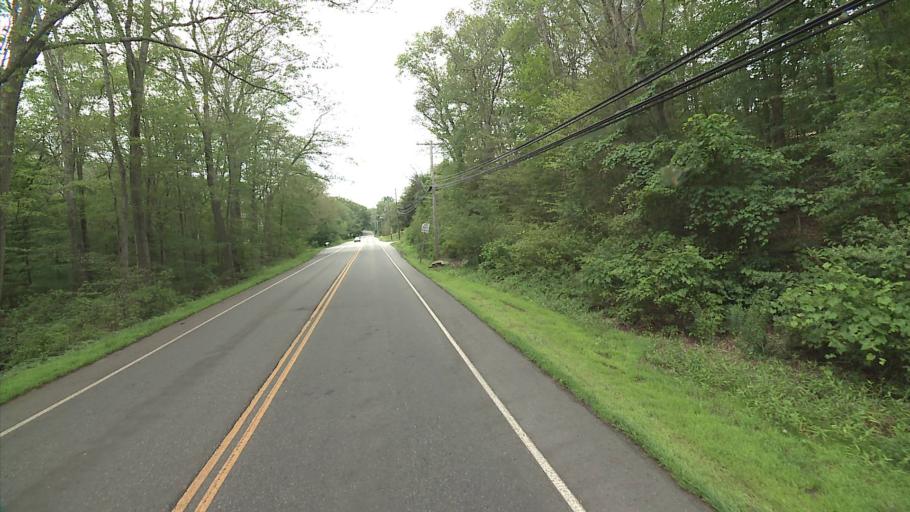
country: US
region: Connecticut
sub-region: New Haven County
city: Guilford
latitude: 41.3517
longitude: -72.6688
